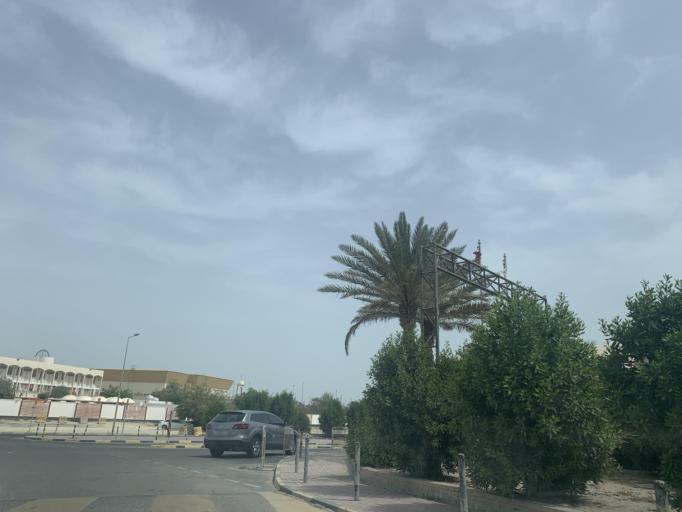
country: BH
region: Northern
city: Madinat `Isa
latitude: 26.1596
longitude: 50.5450
